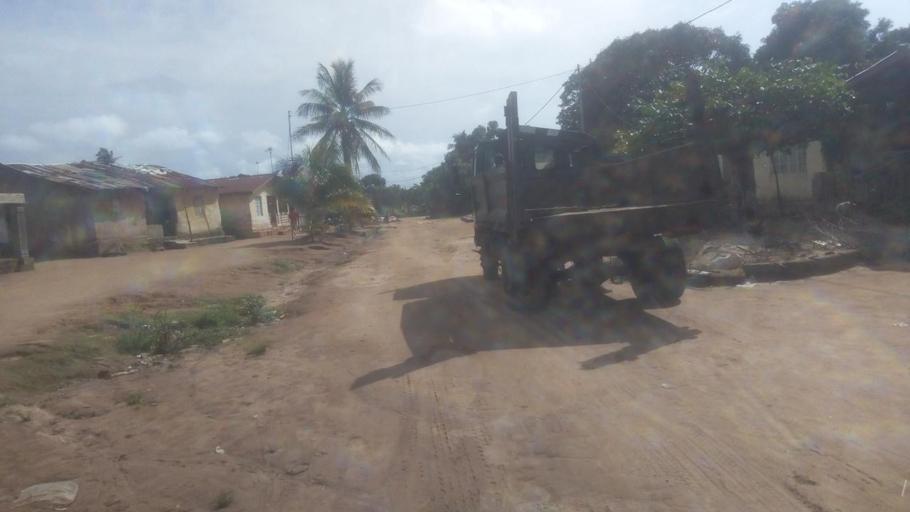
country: SL
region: Northern Province
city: Masoyila
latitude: 8.6120
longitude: -13.1904
